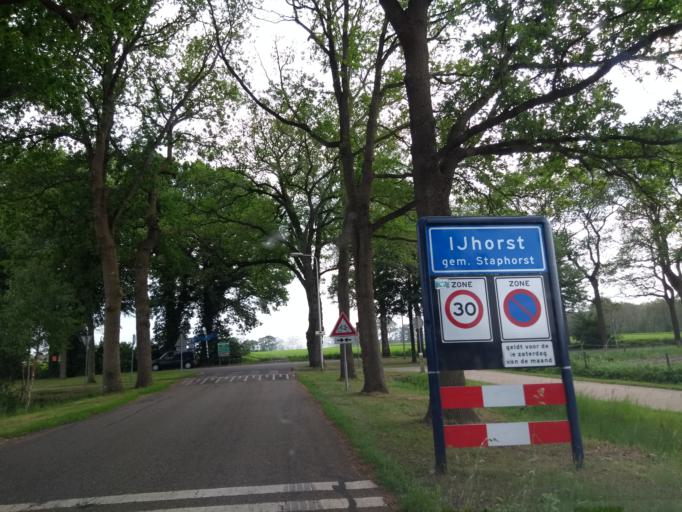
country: NL
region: Overijssel
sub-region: Gemeente Staphorst
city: Staphorst
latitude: 52.6615
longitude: 6.2839
